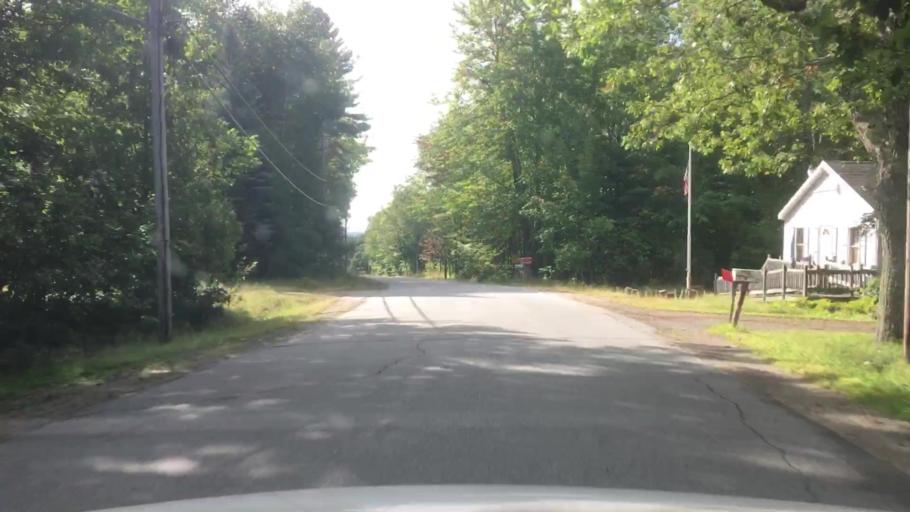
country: US
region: Maine
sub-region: Kennebec County
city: Gardiner
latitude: 44.1791
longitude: -69.8247
